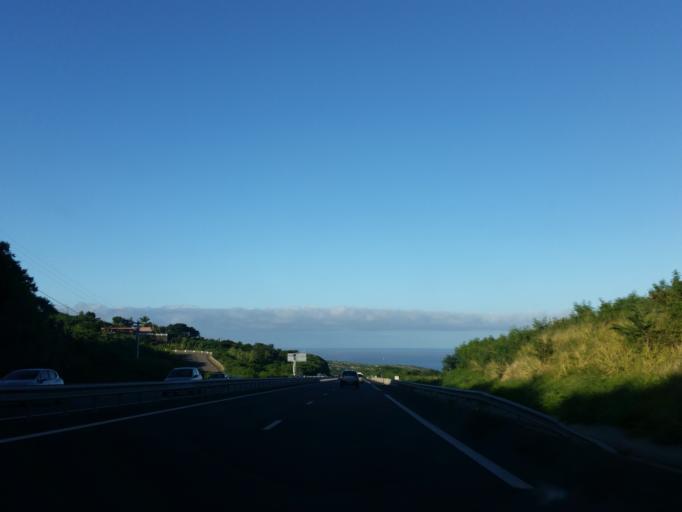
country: RE
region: Reunion
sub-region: Reunion
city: Saint-Leu
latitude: -21.1737
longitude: 55.2978
